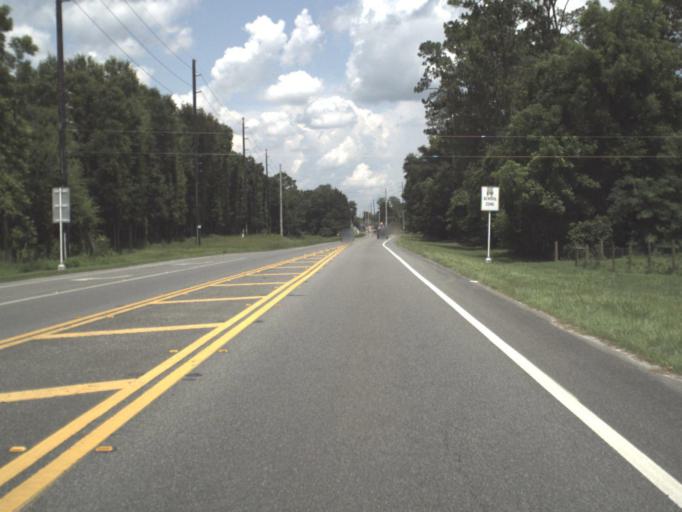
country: US
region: Florida
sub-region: Gilchrist County
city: Trenton
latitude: 29.6134
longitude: -82.8279
